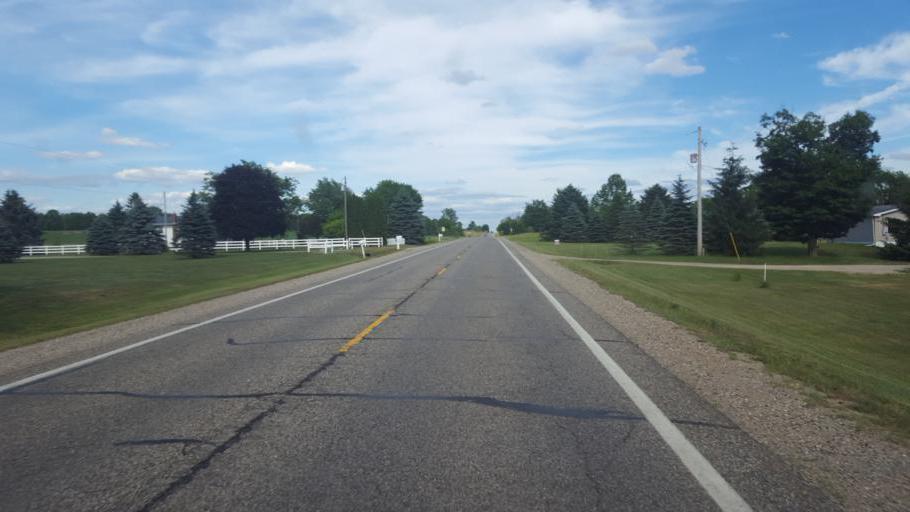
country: US
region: Michigan
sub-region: Eaton County
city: Charlotte
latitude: 42.5678
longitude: -84.9577
